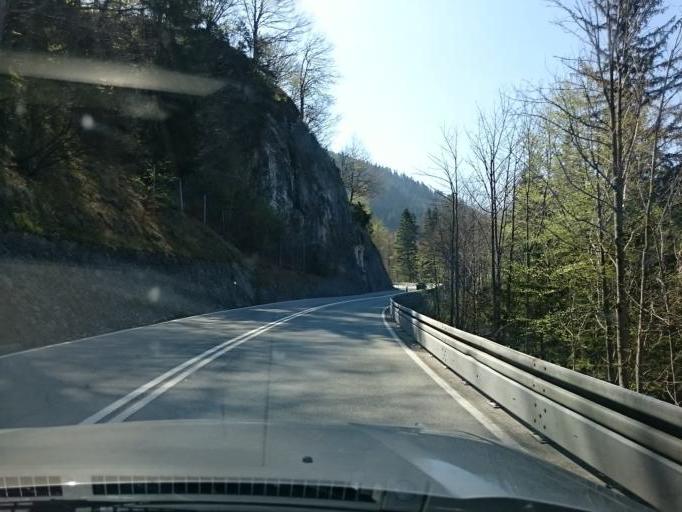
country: DE
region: Bavaria
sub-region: Upper Bavaria
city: Kochel
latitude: 47.6316
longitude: 11.3539
